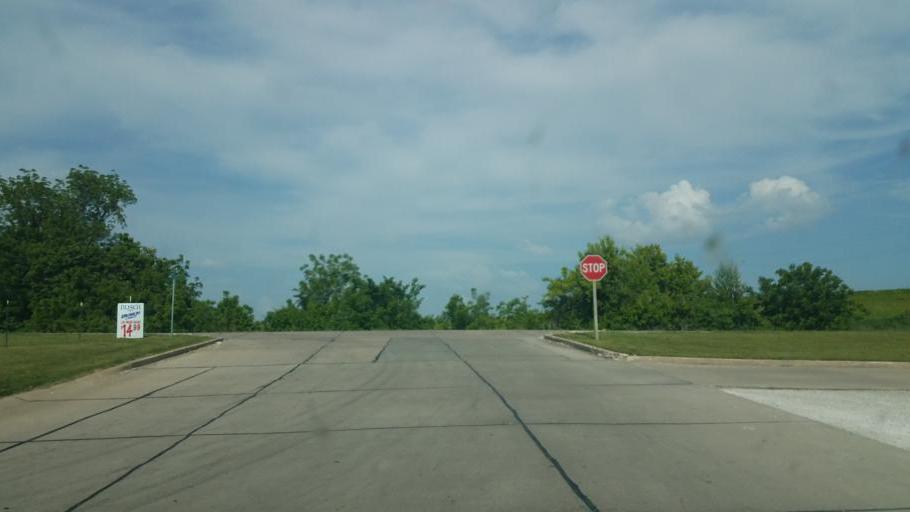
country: US
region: Missouri
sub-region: Cooper County
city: Boonville
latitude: 38.9353
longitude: -92.6912
